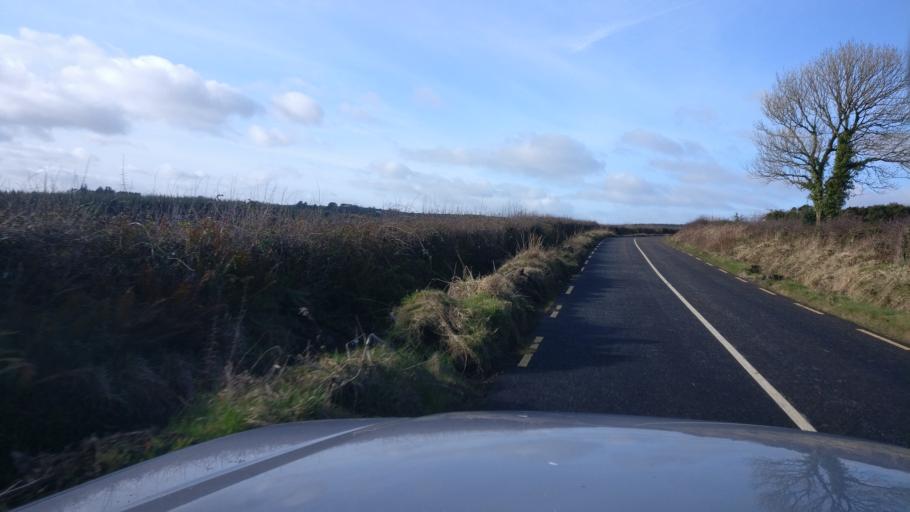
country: IE
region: Leinster
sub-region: Kilkenny
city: Castlecomer
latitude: 52.9036
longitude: -7.1792
